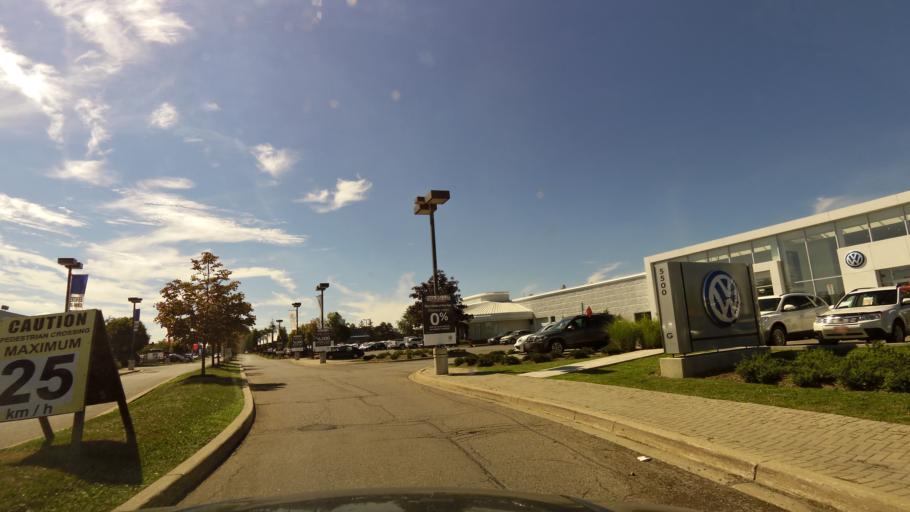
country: CA
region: Ontario
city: Mississauga
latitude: 43.6453
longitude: -79.6365
